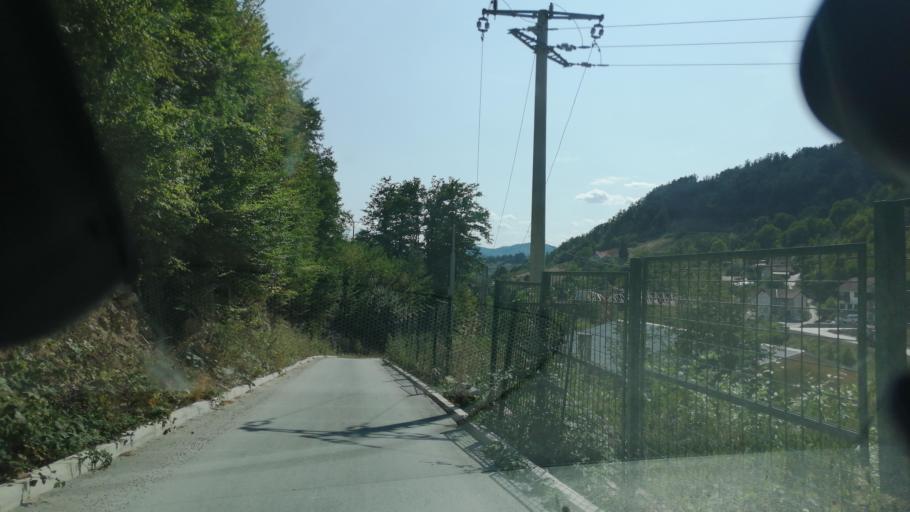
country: RS
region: Central Serbia
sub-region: Moravicki Okrug
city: Ivanjica
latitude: 43.6258
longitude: 20.2414
